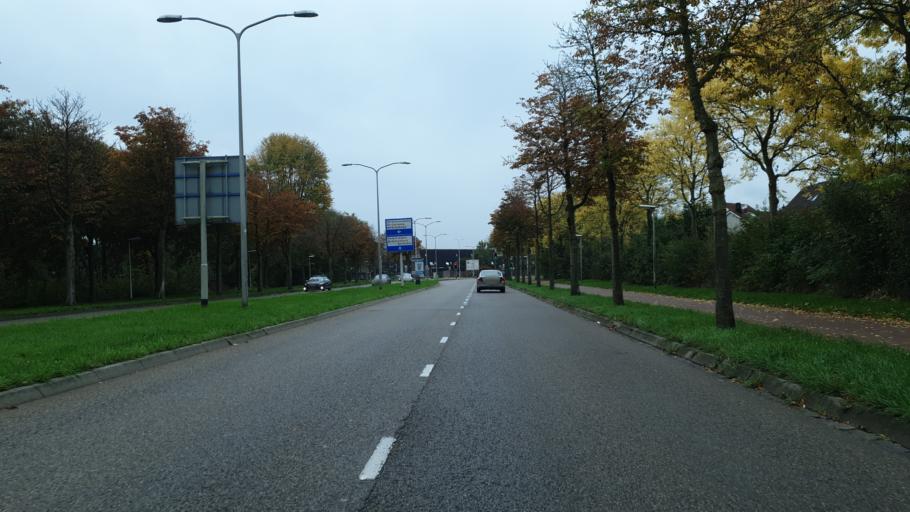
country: NL
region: Gelderland
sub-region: Gemeente Nijmegen
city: Lindenholt
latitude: 51.8314
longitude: 5.7961
